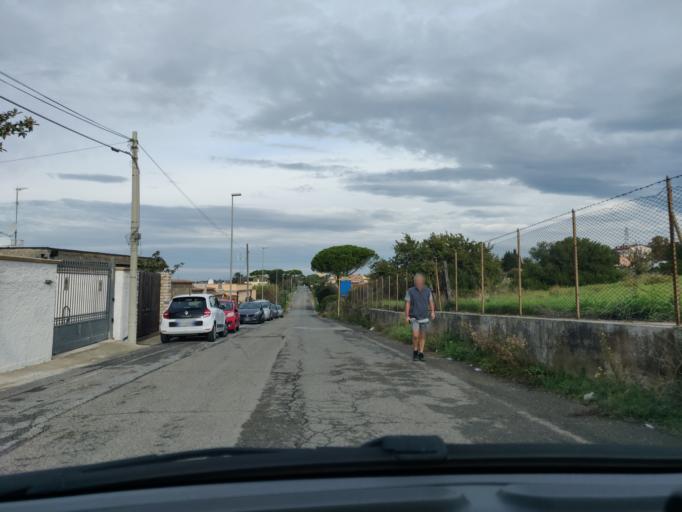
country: IT
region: Latium
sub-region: Citta metropolitana di Roma Capitale
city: Civitavecchia
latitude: 42.1001
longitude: 11.8135
